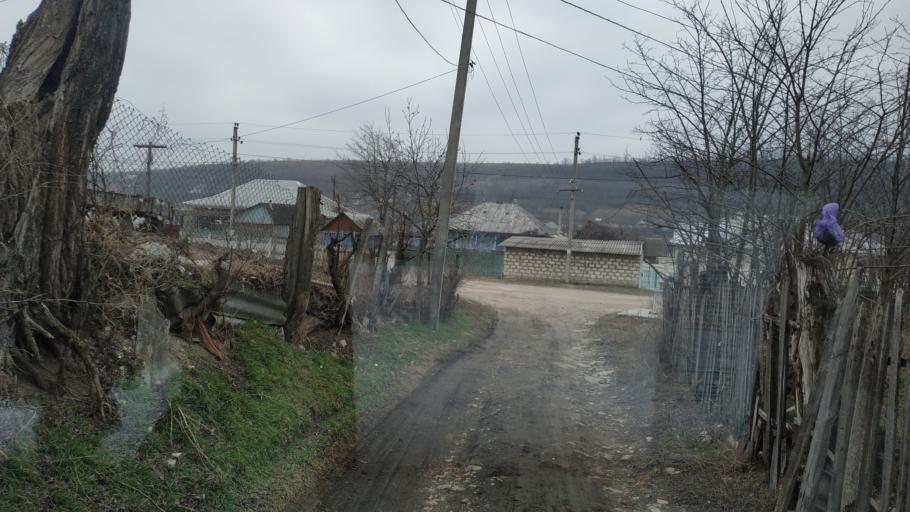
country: MD
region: Hincesti
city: Hincesti
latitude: 46.8900
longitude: 28.4055
